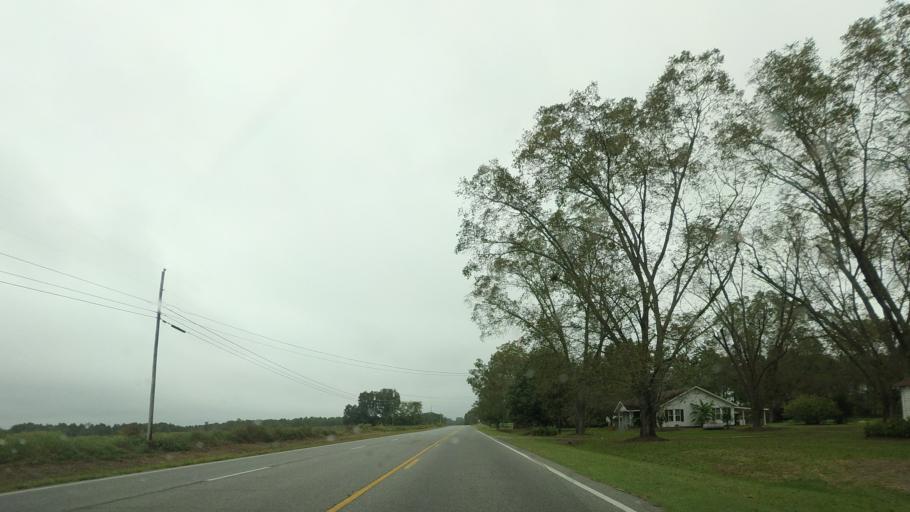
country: US
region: Georgia
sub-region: Ben Hill County
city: Fitzgerald
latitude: 31.6715
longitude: -83.2356
